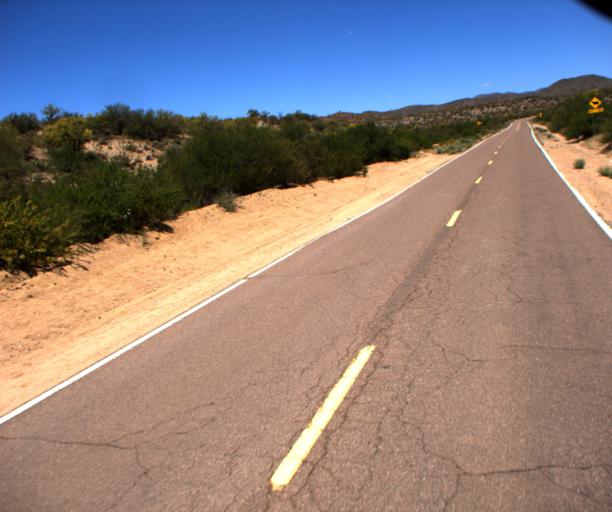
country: US
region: Arizona
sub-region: Yavapai County
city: Bagdad
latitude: 34.4443
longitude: -113.2421
